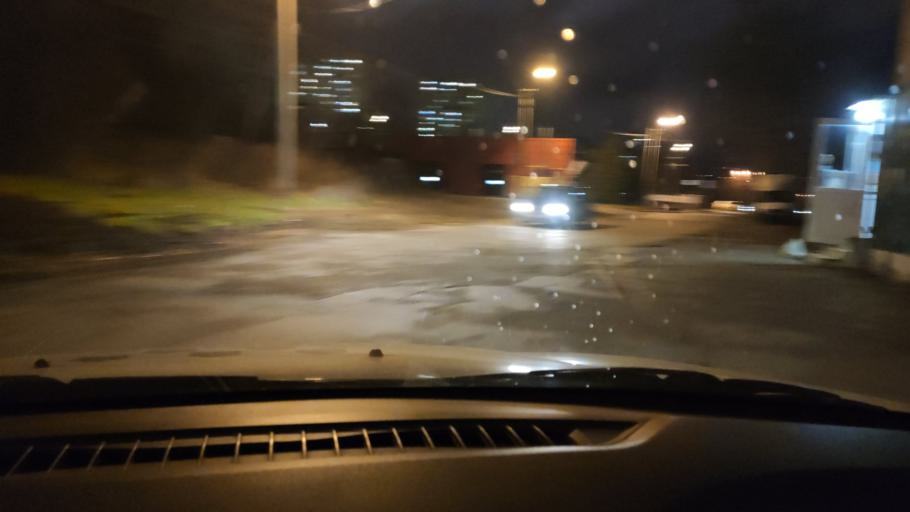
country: RU
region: Perm
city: Perm
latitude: 58.0012
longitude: 56.2057
